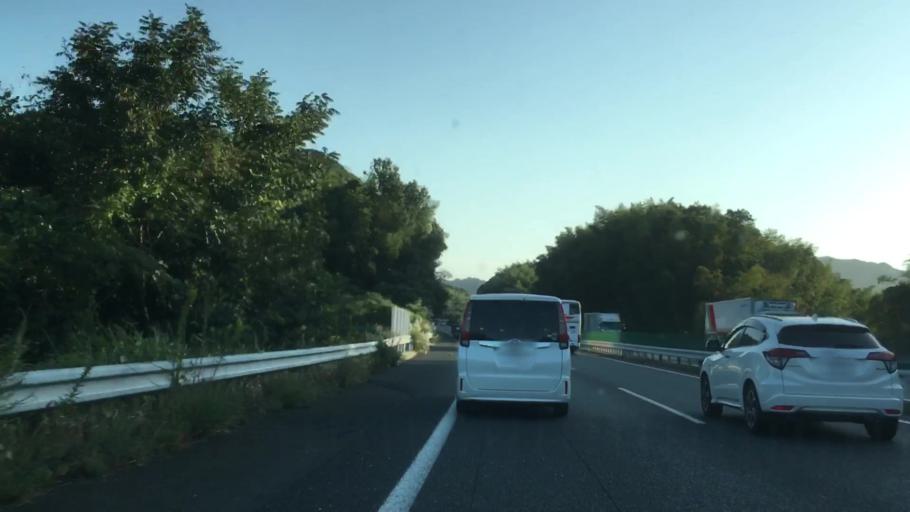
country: JP
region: Yamaguchi
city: Shimonoseki
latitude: 34.0585
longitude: 131.0078
